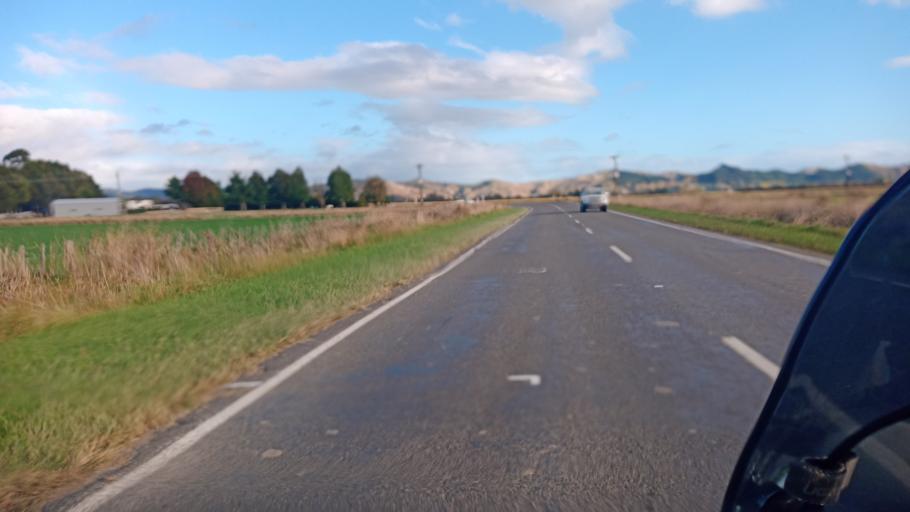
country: NZ
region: Gisborne
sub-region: Gisborne District
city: Gisborne
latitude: -38.6348
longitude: 177.9068
